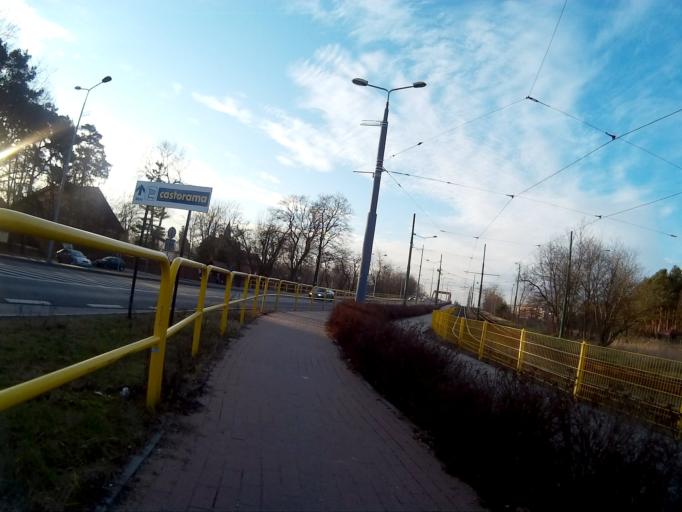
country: PL
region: Kujawsko-Pomorskie
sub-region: Bydgoszcz
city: Bydgoszcz
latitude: 53.1492
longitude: 18.0271
